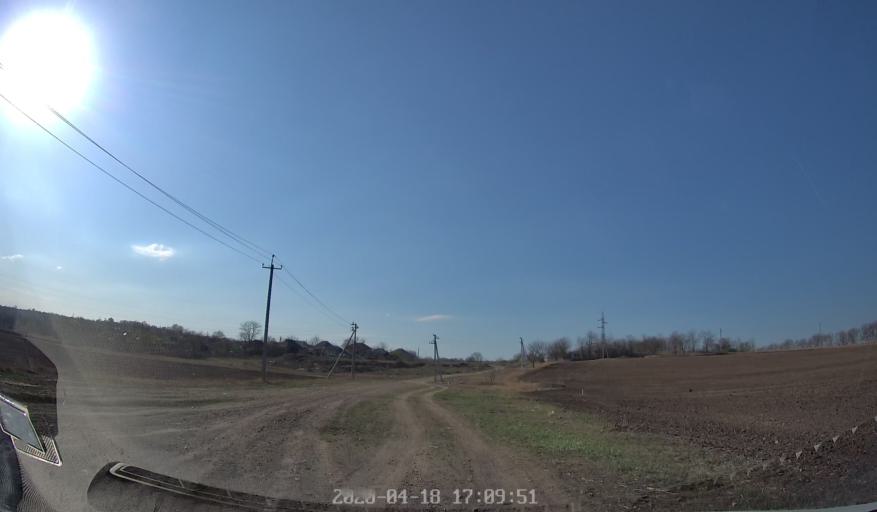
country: MD
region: Chisinau
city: Vadul lui Voda
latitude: 47.1479
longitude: 29.0865
